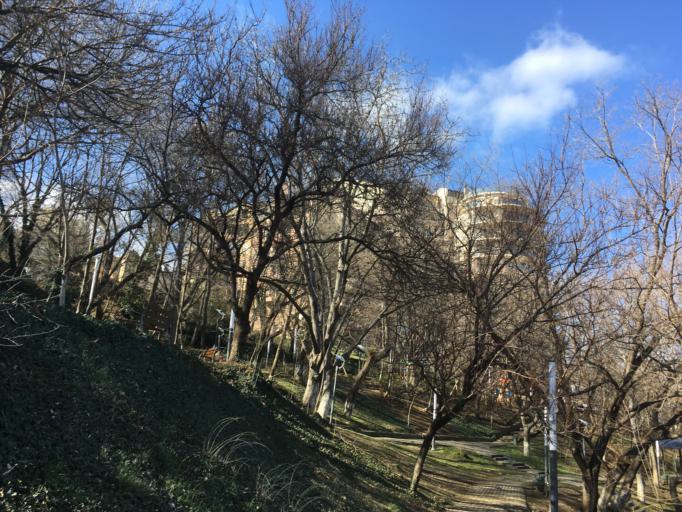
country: GE
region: T'bilisi
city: Tbilisi
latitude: 41.7114
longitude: 44.7699
